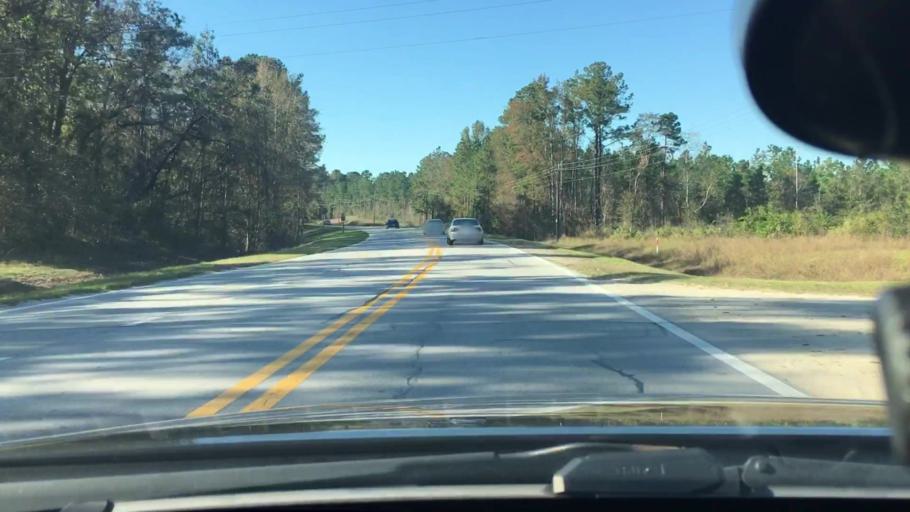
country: US
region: North Carolina
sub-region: Craven County
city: Vanceboro
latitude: 35.2177
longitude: -77.1215
